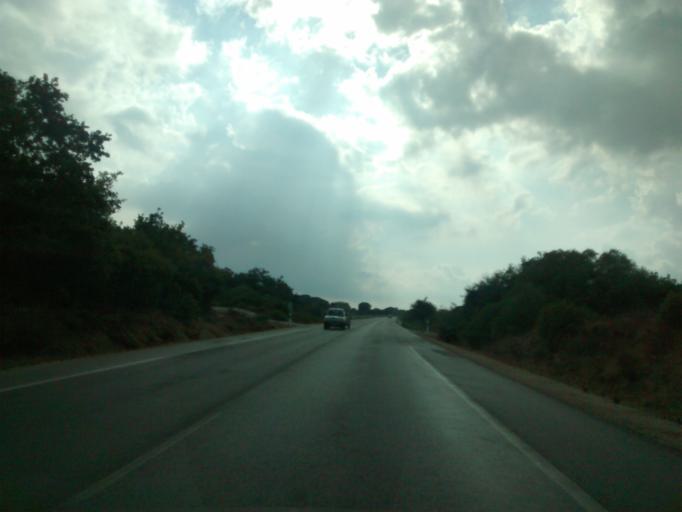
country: ES
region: Andalusia
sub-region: Provincia de Cadiz
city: Bornos
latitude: 36.7547
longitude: -5.7128
